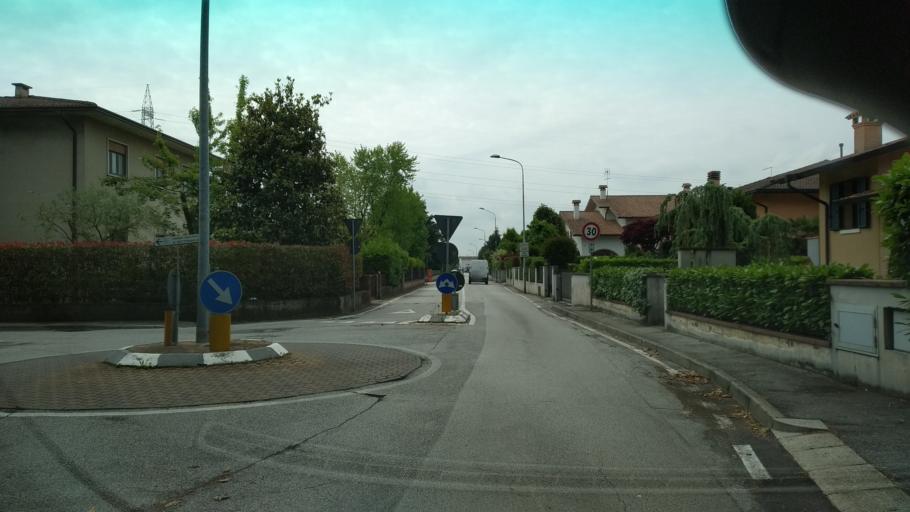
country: IT
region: Veneto
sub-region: Provincia di Vicenza
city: Caldogno-Rettorgole-Cresole
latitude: 45.5939
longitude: 11.5205
